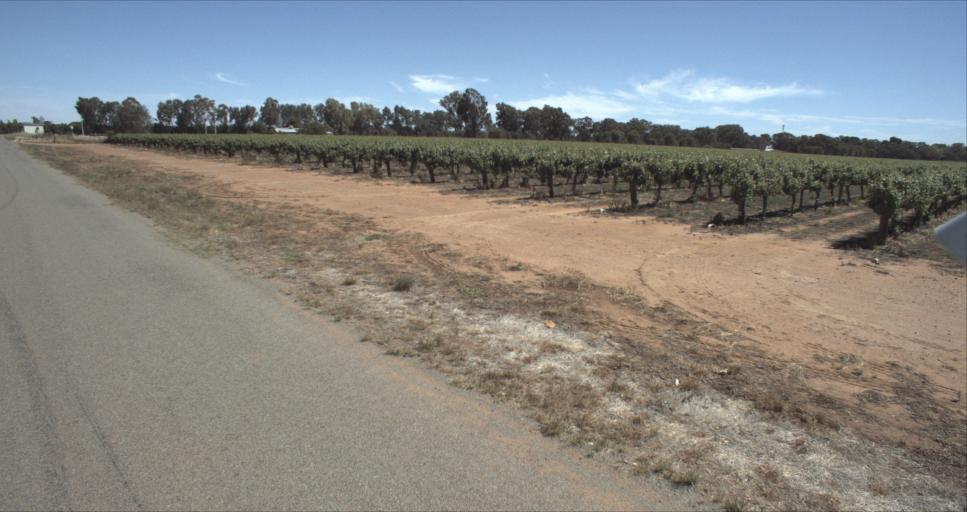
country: AU
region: New South Wales
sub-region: Leeton
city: Leeton
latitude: -34.5304
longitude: 146.3458
